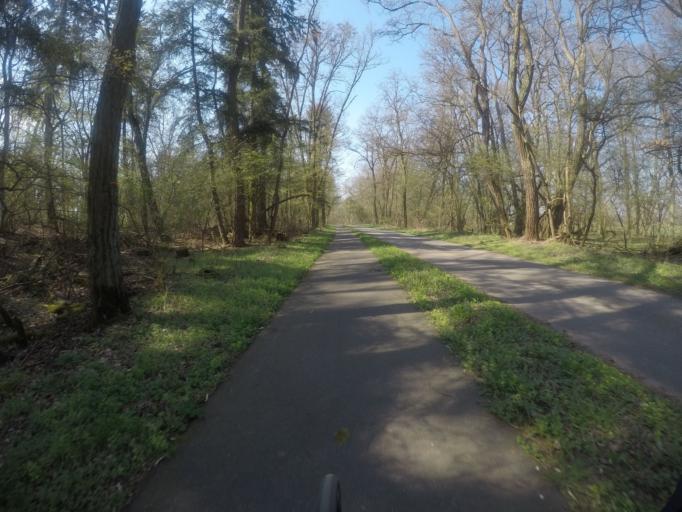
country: DE
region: Brandenburg
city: Nauen
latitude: 52.6596
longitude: 12.9274
